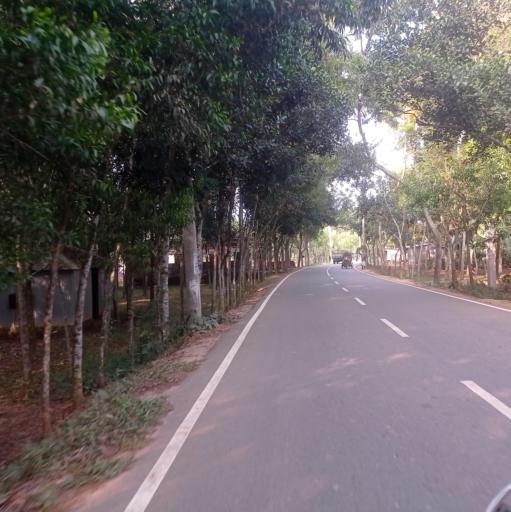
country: BD
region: Dhaka
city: Bhairab Bazar
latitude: 24.0687
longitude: 90.8417
